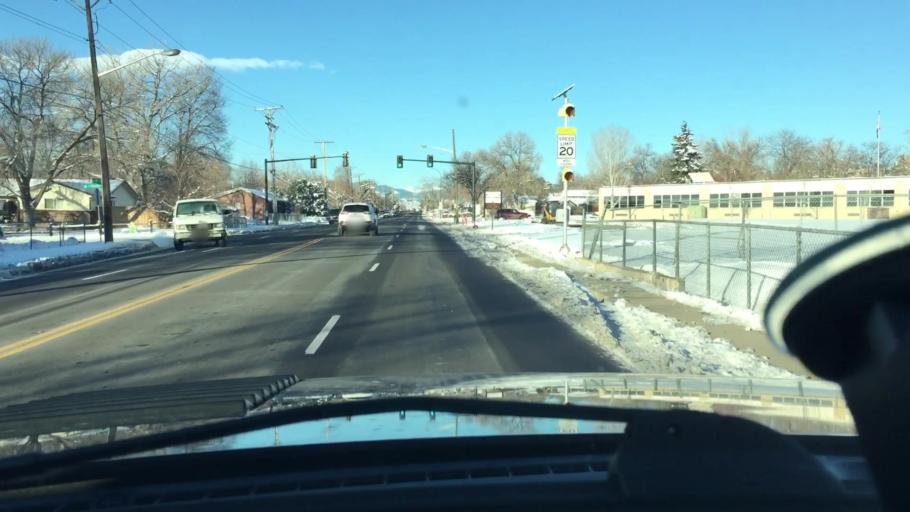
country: US
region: Colorado
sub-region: Adams County
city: Westminster
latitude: 39.8418
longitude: -105.0281
